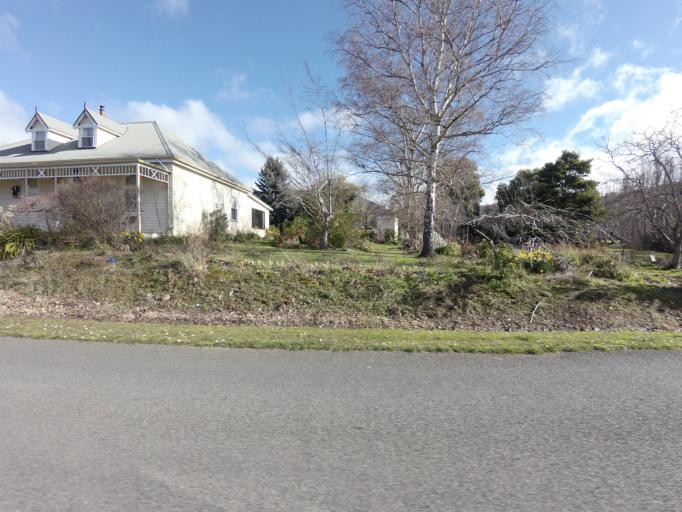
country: AU
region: Tasmania
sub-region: Derwent Valley
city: New Norfolk
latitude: -42.6502
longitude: 146.7677
